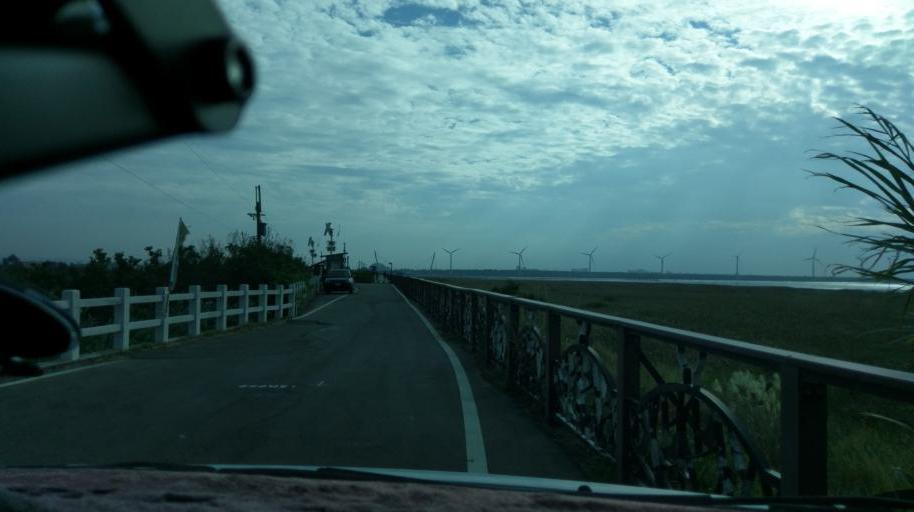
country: TW
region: Taiwan
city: Fengyuan
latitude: 24.3213
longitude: 120.5526
